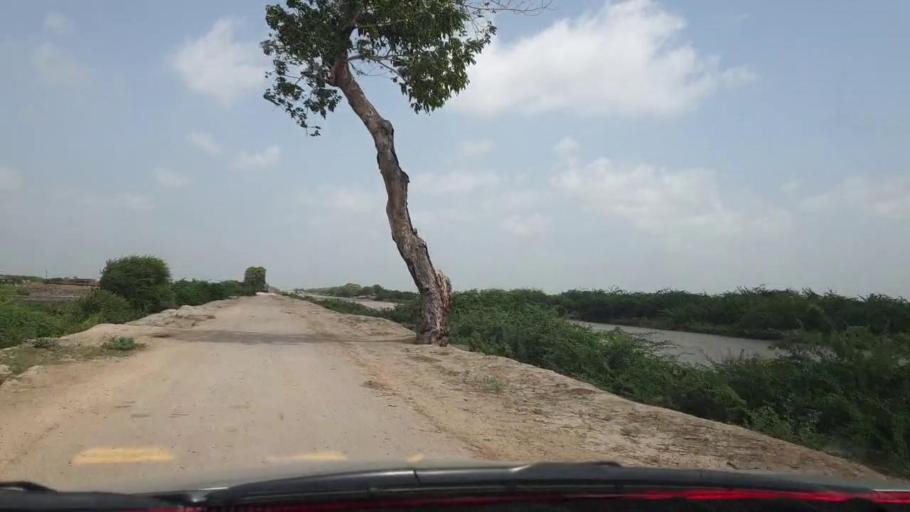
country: PK
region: Sindh
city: Talhar
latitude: 24.8928
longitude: 68.8354
